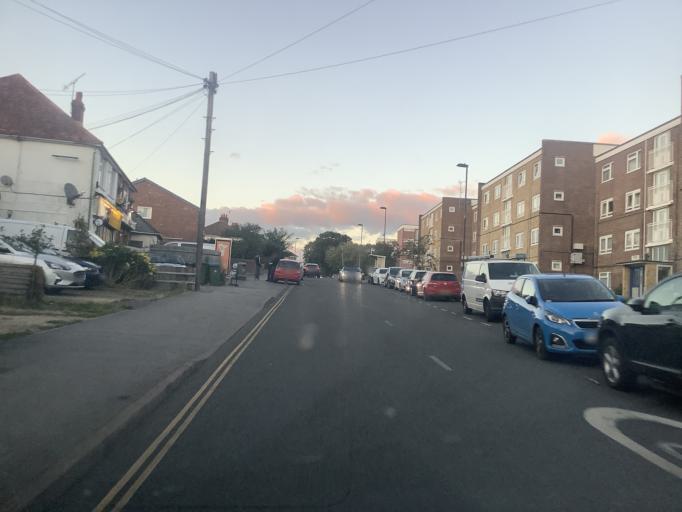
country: GB
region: England
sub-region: Hampshire
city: Marchwood
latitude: 50.9277
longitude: -1.4510
